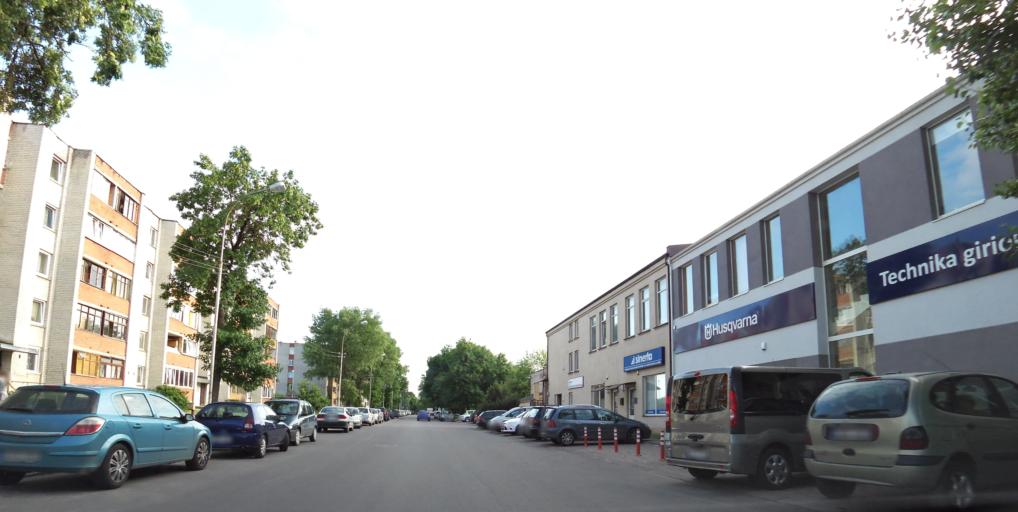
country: LT
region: Vilnius County
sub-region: Vilnius
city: Vilnius
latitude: 54.7110
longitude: 25.2910
